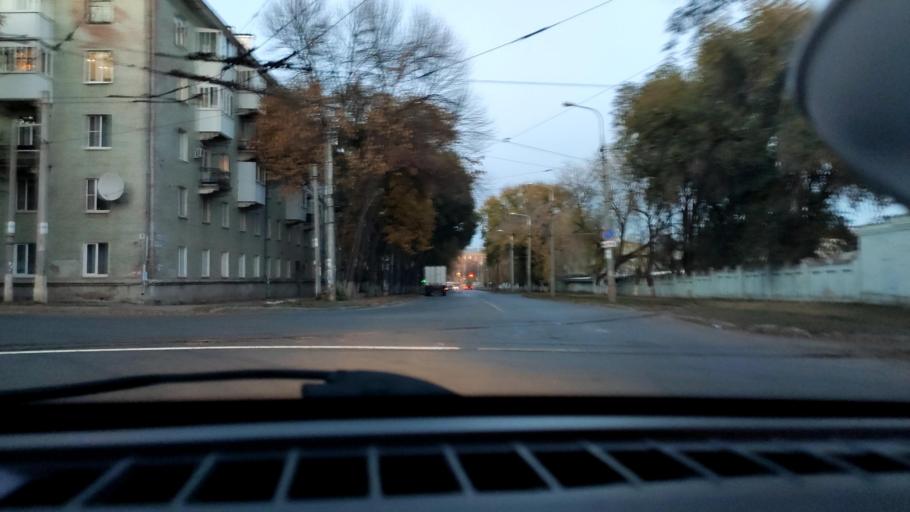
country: RU
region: Samara
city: Samara
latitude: 53.2037
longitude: 50.2323
